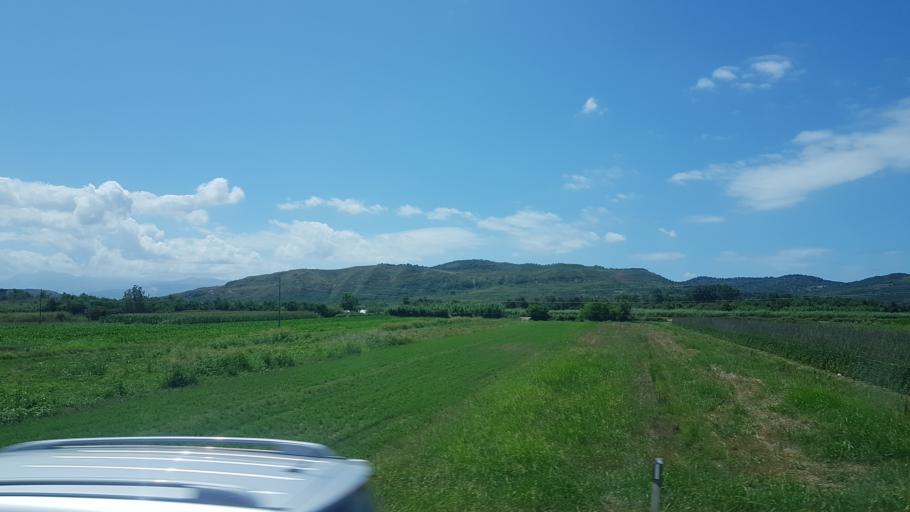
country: AL
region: Fier
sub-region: Rrethi i Fierit
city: Frakulla e Madhe
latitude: 40.6088
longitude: 19.5335
